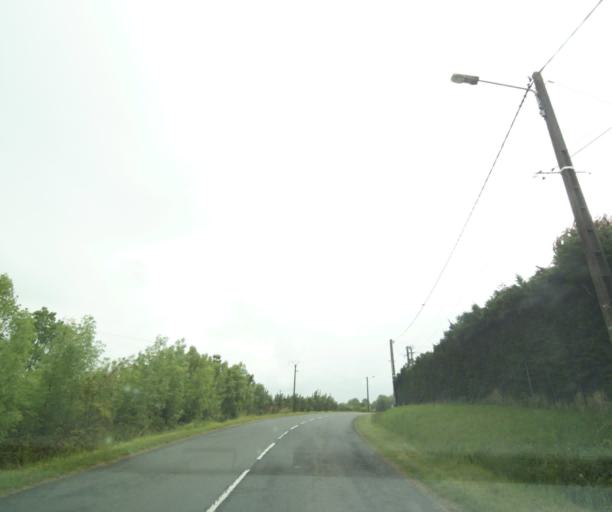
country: FR
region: Poitou-Charentes
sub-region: Departement de la Charente-Maritime
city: Chaniers
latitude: 45.7623
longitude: -0.5346
